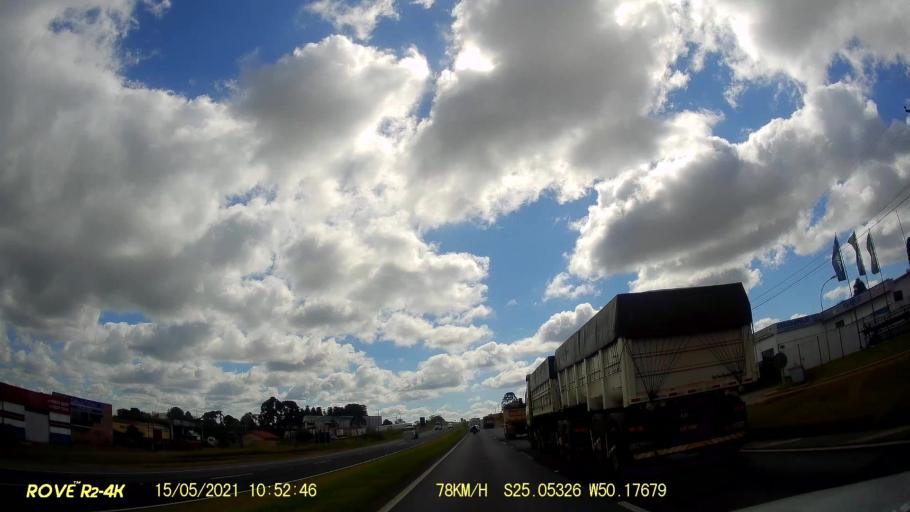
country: BR
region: Parana
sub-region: Ponta Grossa
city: Ponta Grossa
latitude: -25.0534
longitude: -50.1768
